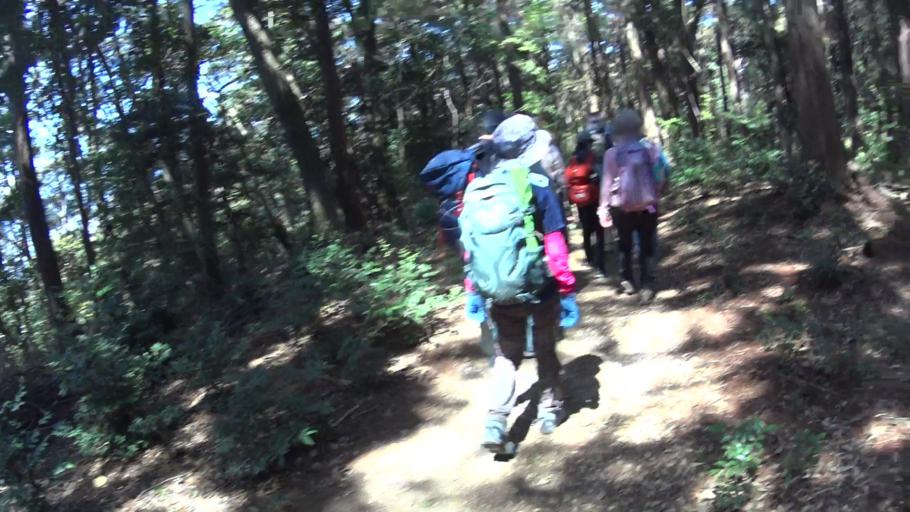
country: JP
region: Kyoto
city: Kyoto
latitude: 34.9964
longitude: 135.7875
